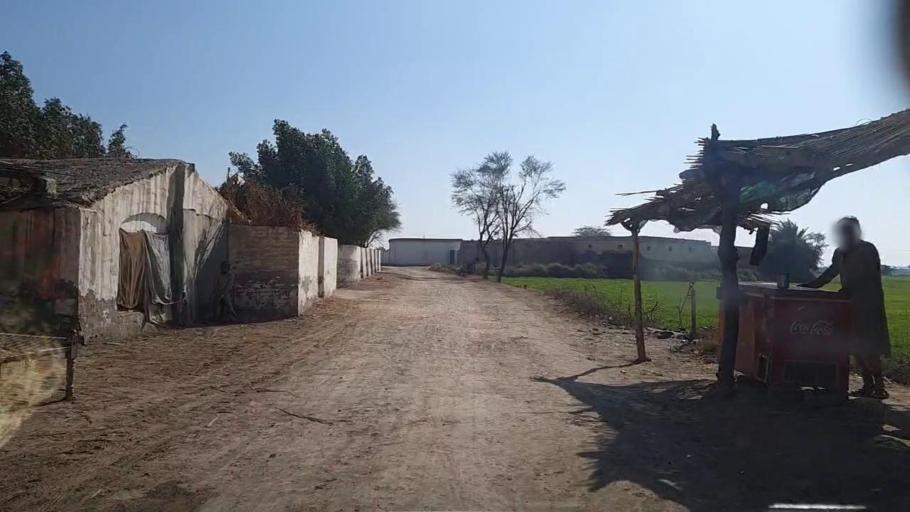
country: PK
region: Sindh
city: Khairpur
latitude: 28.0469
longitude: 69.7814
